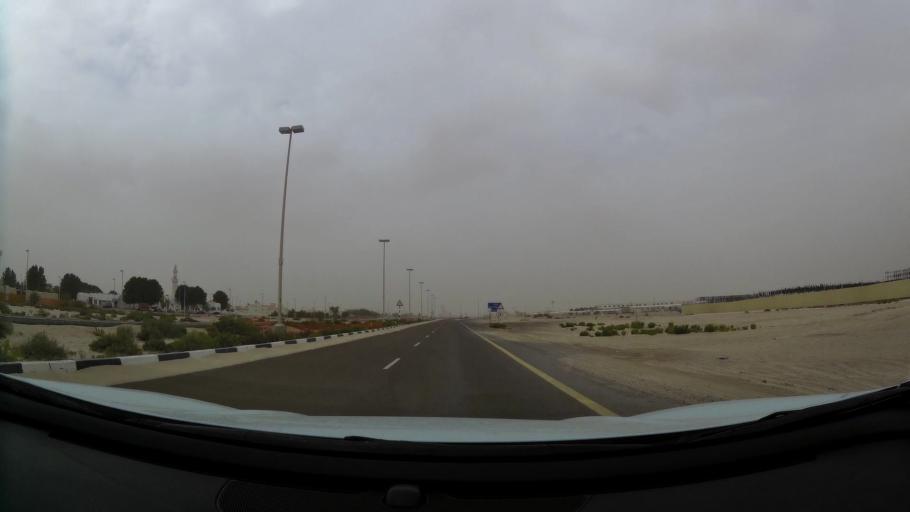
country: AE
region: Abu Dhabi
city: Abu Dhabi
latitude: 24.4307
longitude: 54.7502
